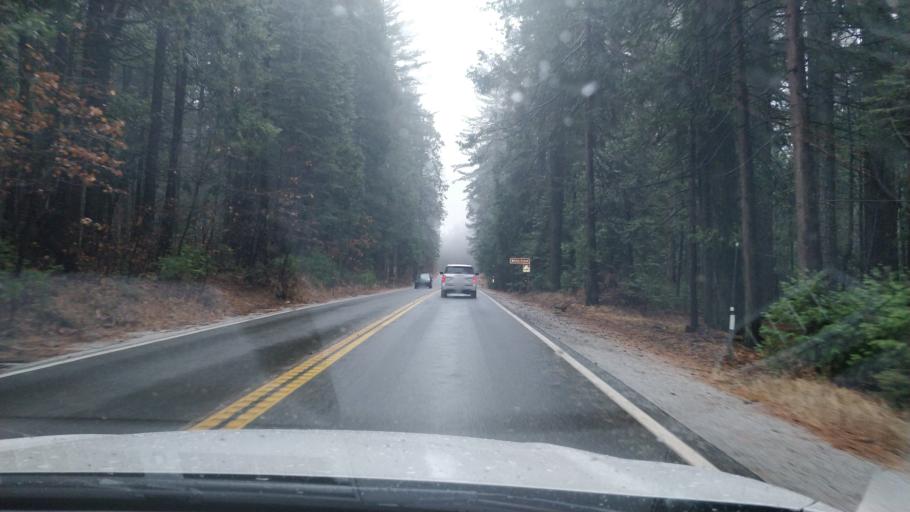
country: US
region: California
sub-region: Nevada County
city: Nevada City
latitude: 39.3218
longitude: -120.8500
